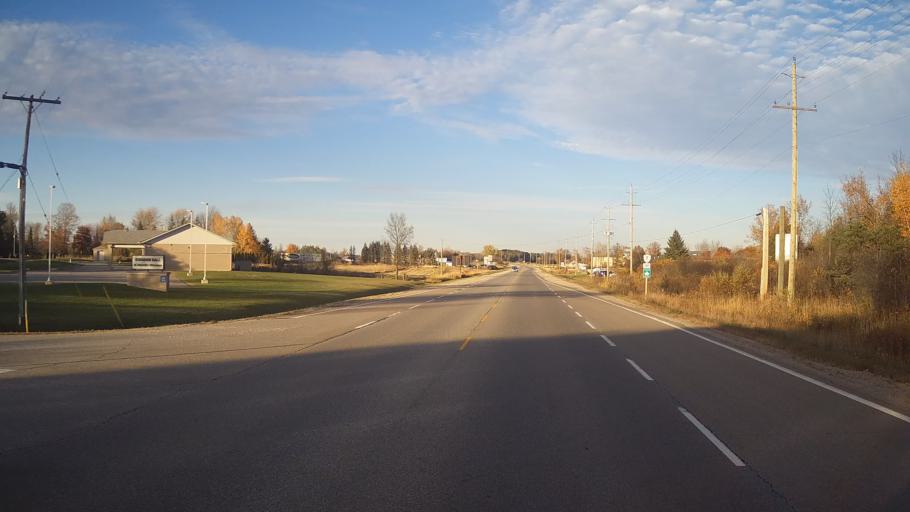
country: CA
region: Ontario
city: Perth
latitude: 44.9280
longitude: -76.2471
